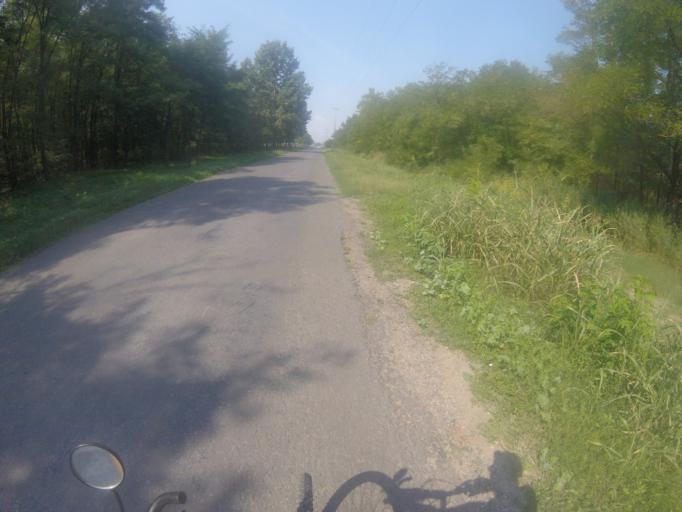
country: HU
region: Bacs-Kiskun
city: Ersekcsanad
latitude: 46.2547
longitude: 18.9580
